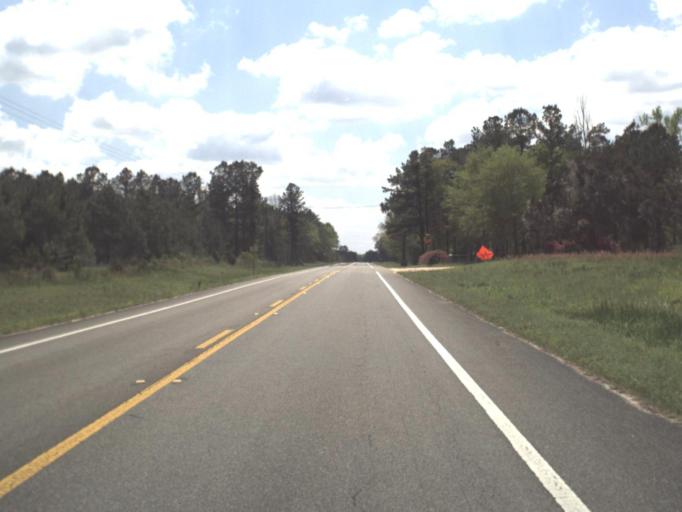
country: US
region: Florida
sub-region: Okaloosa County
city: Crestview
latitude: 30.9451
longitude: -86.6343
